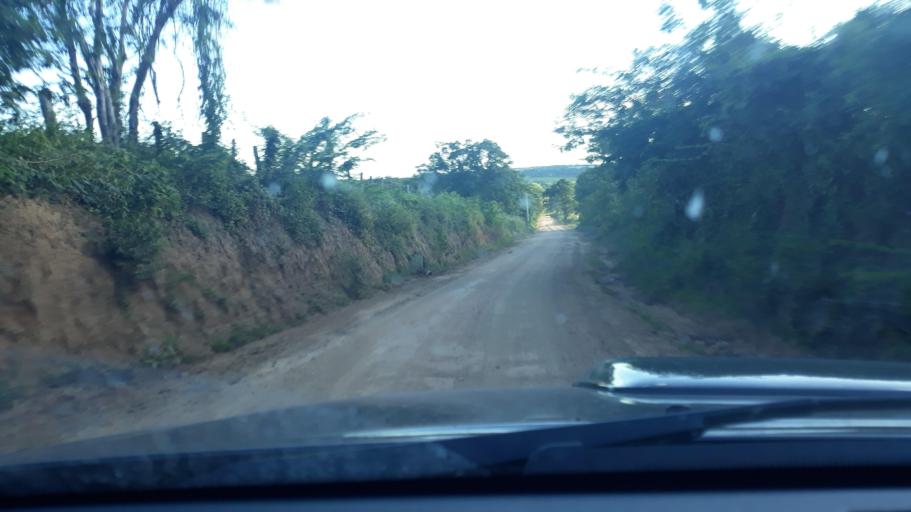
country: BR
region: Bahia
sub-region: Riacho De Santana
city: Riacho de Santana
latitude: -13.8203
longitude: -42.7241
